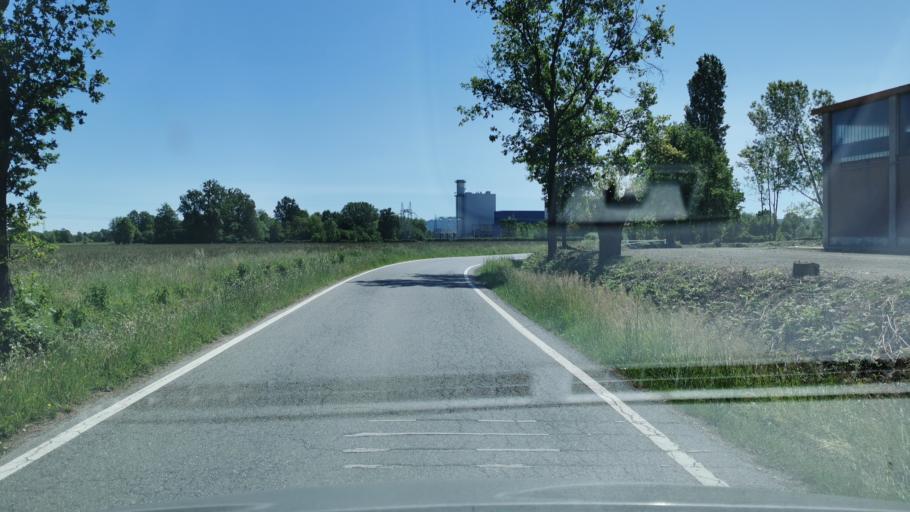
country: IT
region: Piedmont
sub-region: Provincia di Torino
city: Settimo Torinese
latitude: 45.1649
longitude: 7.7431
